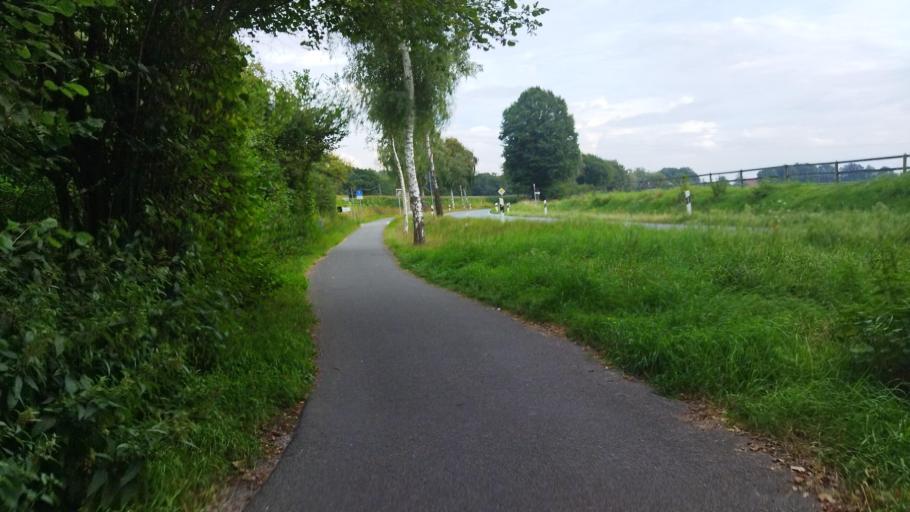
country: DE
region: North Rhine-Westphalia
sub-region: Regierungsbezirk Munster
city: Telgte
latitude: 51.9980
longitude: 7.7612
